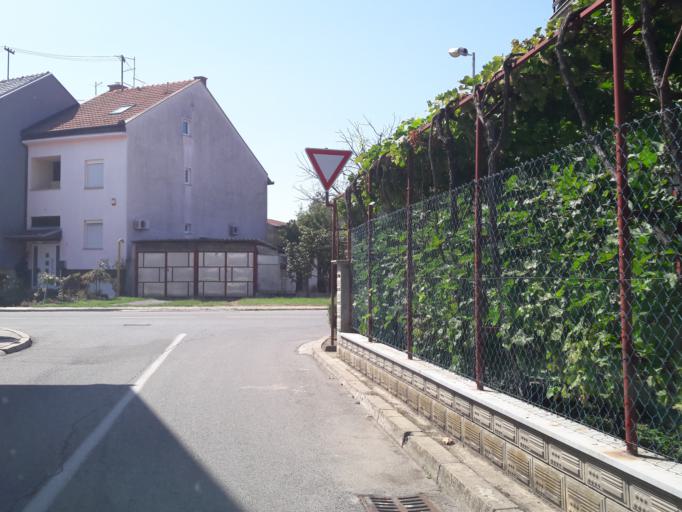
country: HR
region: Osjecko-Baranjska
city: Visnjevac
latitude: 45.5593
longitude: 18.6517
